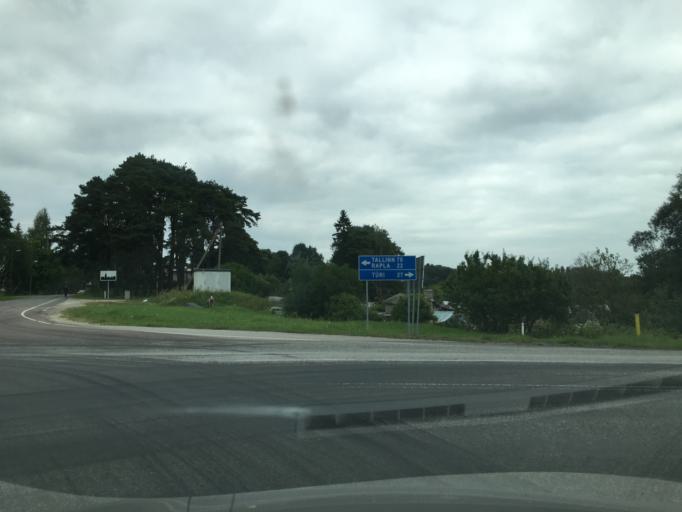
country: EE
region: Raplamaa
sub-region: Kehtna vald
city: Kehtna
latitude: 58.8592
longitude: 24.9987
